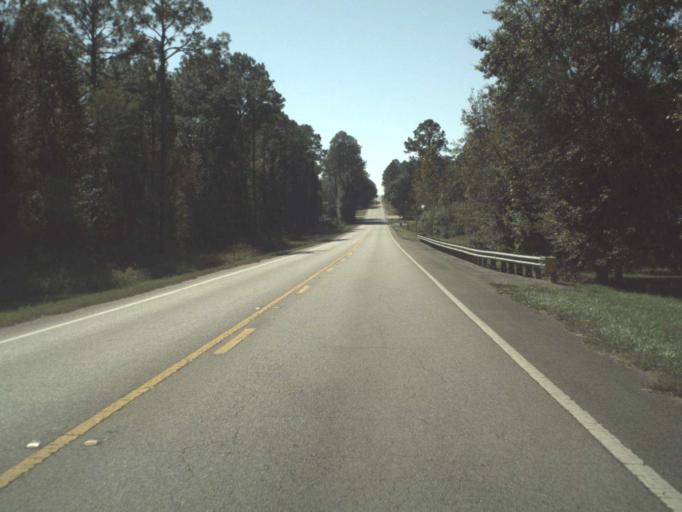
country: US
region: Alabama
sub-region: Geneva County
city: Samson
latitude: 30.9748
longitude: -86.1351
